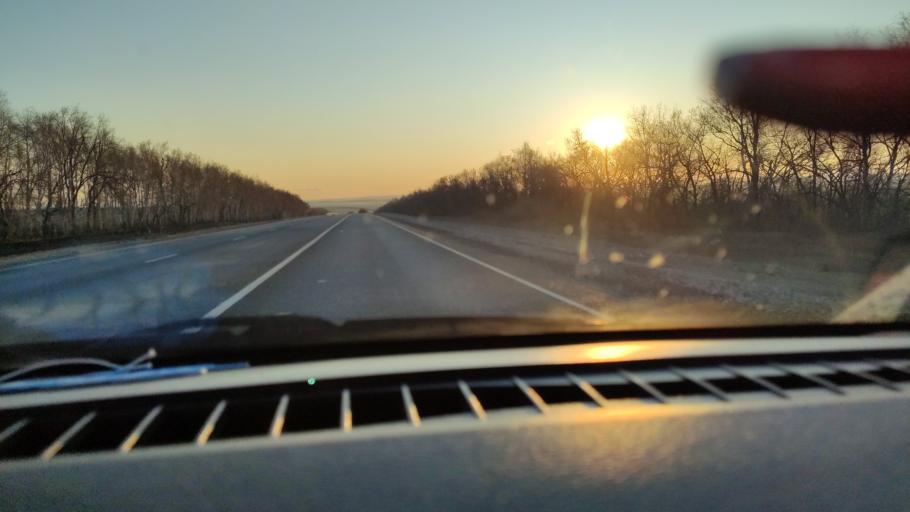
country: RU
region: Saratov
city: Sinodskoye
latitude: 51.8996
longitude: 46.5392
